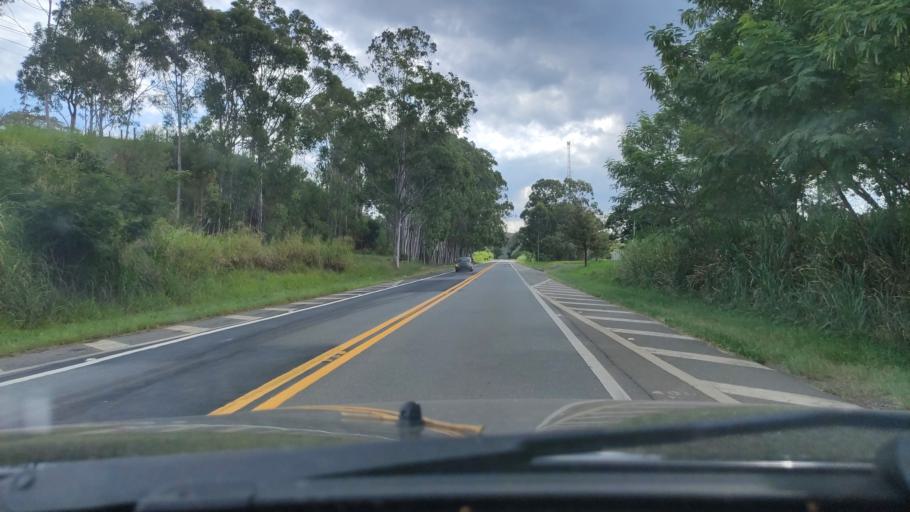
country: BR
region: Sao Paulo
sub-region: Itapira
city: Itapira
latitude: -22.4599
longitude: -46.7350
